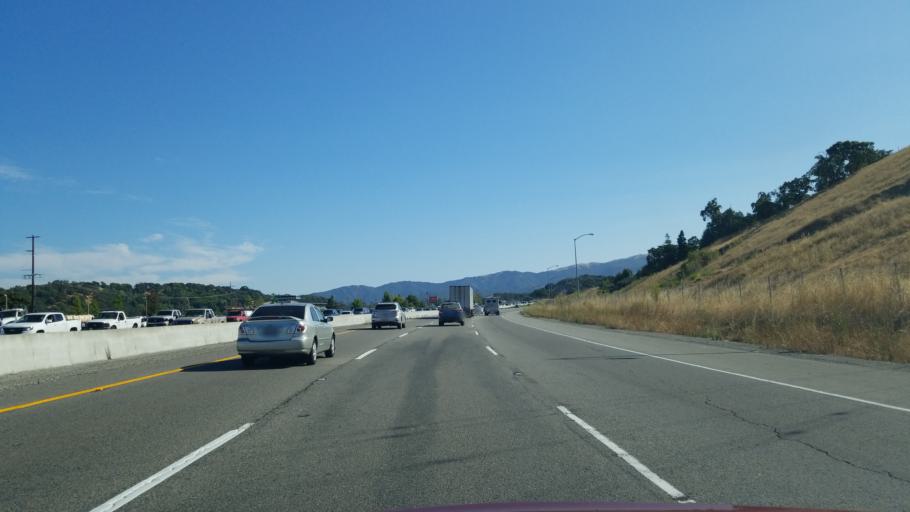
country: US
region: California
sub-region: Marin County
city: Novato
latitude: 38.1311
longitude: -122.5641
